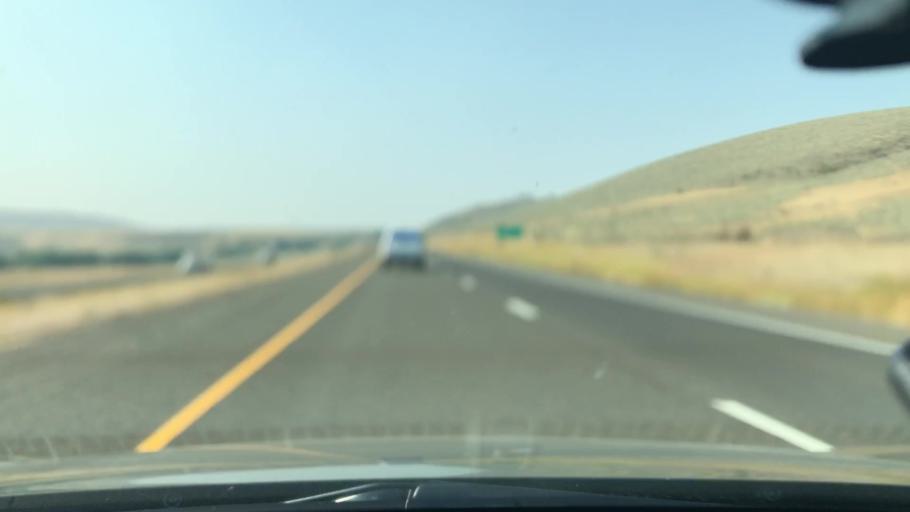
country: US
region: Oregon
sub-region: Union County
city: Union
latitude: 45.1364
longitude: -117.9670
